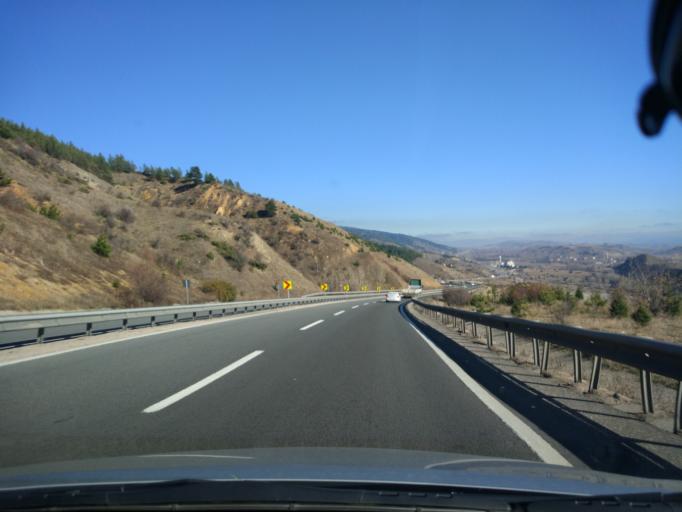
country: TR
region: Karabuk
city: Gozyeri
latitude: 40.8316
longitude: 32.3946
